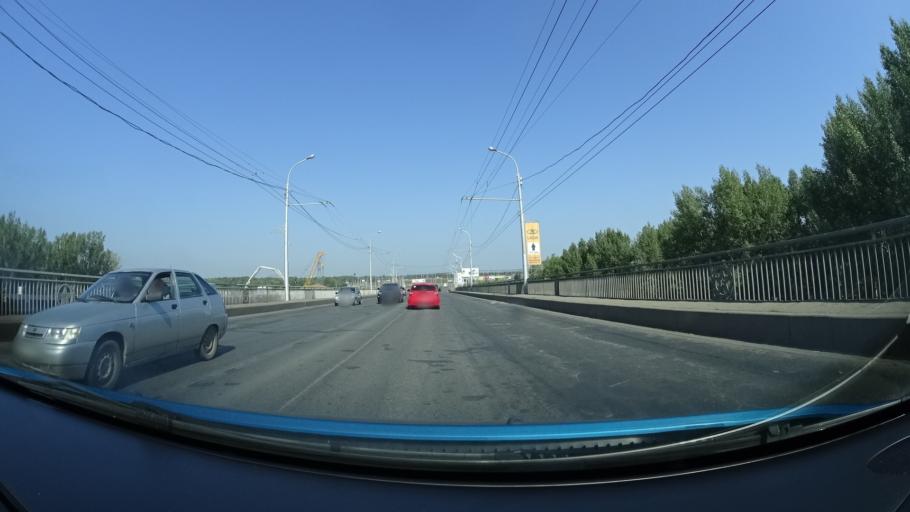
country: RU
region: Bashkortostan
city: Ufa
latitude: 54.7596
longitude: 55.9621
